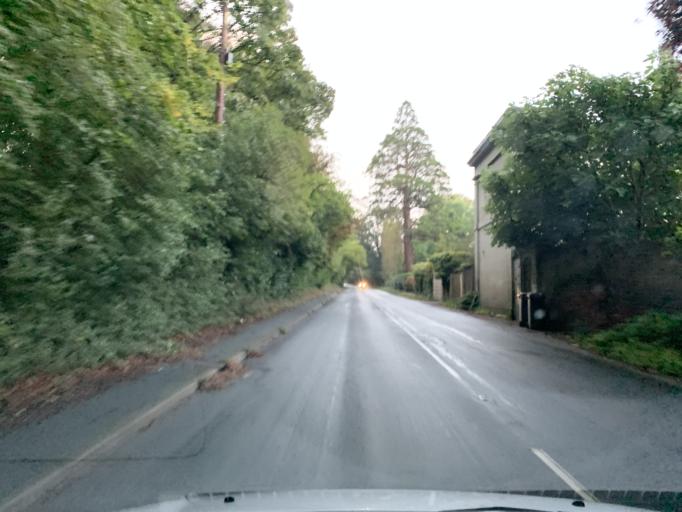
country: GB
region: England
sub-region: Wiltshire
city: Alderbury
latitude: 51.0554
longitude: -1.7571
